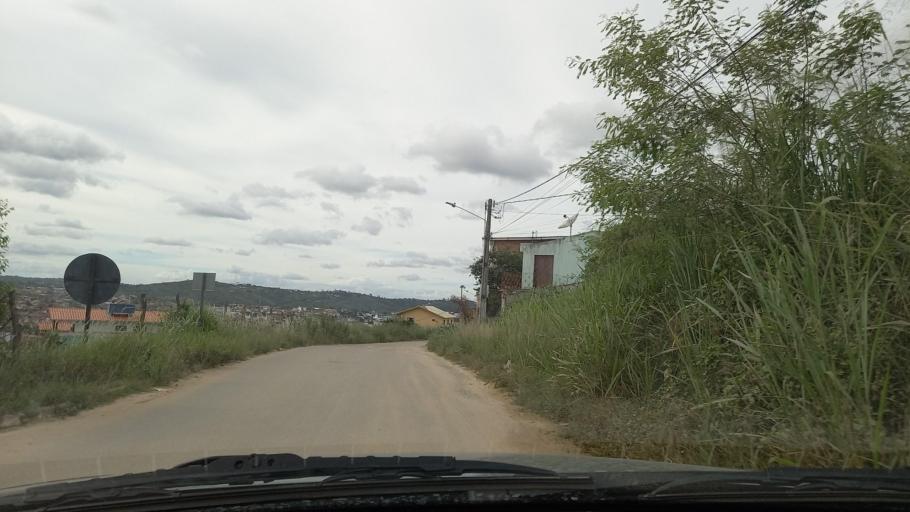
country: BR
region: Pernambuco
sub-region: Gravata
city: Gravata
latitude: -8.2116
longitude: -35.5767
